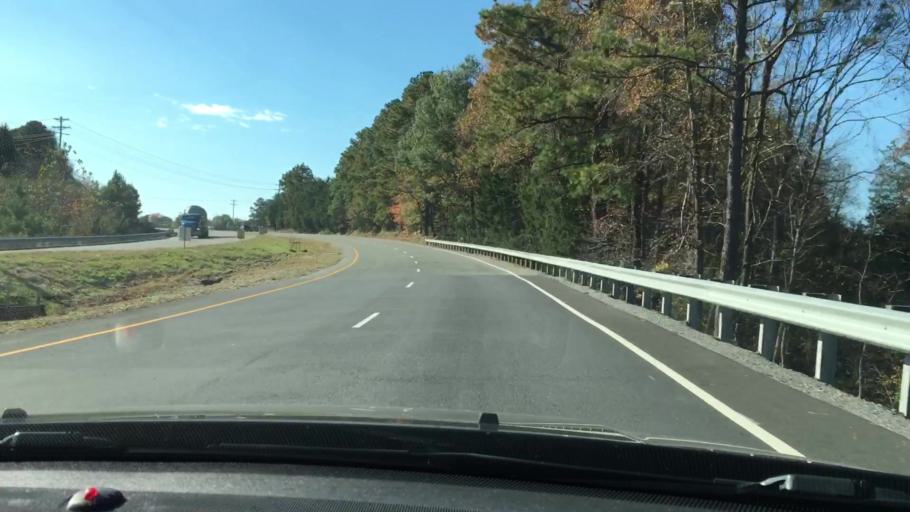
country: US
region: Virginia
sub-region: Hanover County
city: Ashland
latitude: 37.8515
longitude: -77.4334
